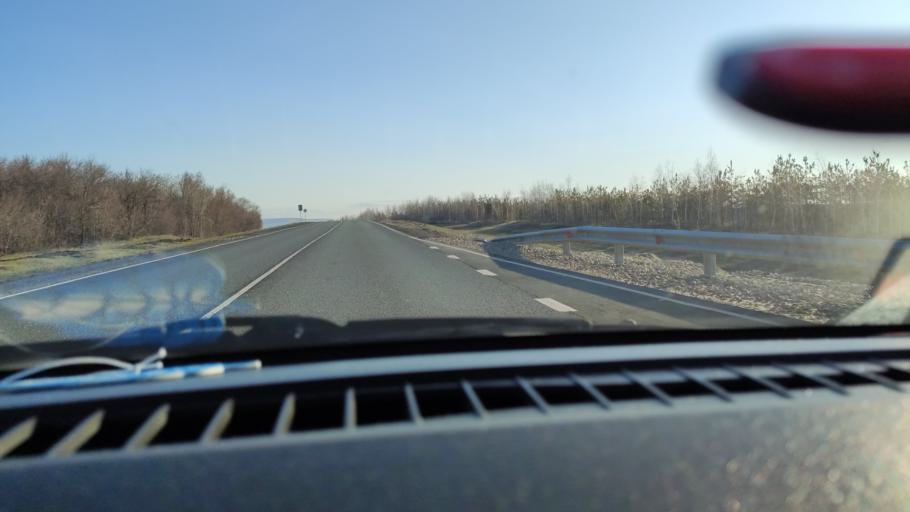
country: RU
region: Saratov
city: Balakovo
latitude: 52.1619
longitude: 47.8225
